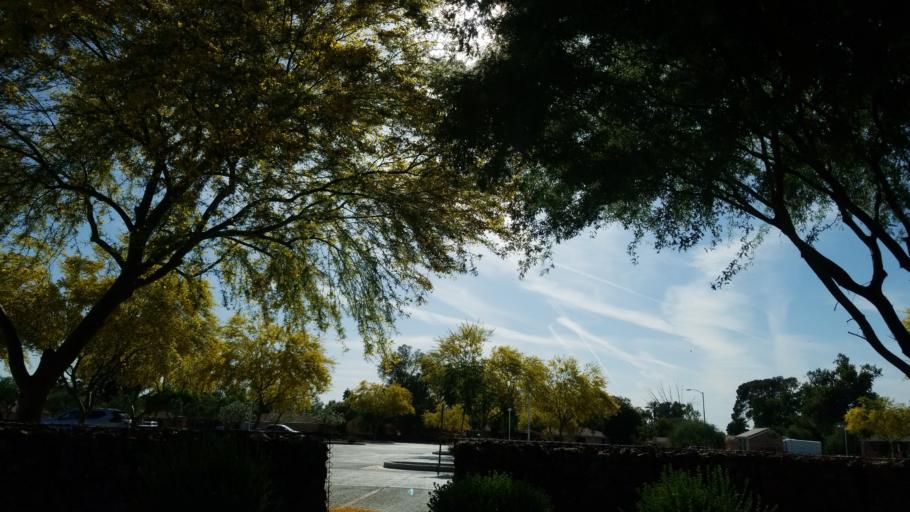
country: US
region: Arizona
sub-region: Maricopa County
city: Queen Creek
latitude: 33.3109
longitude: -111.6792
